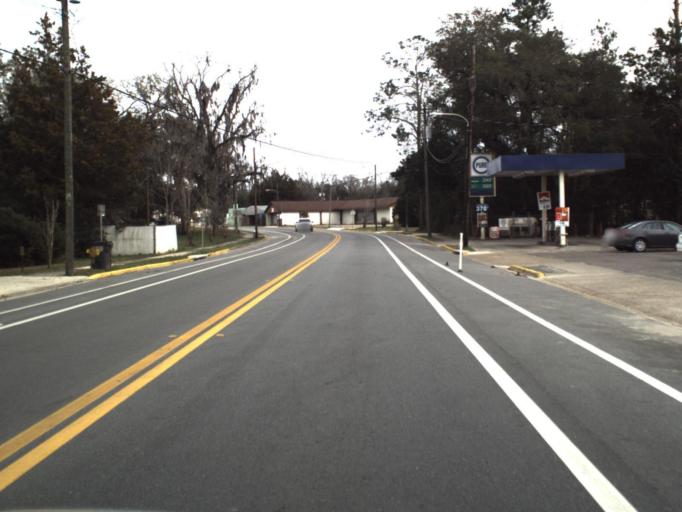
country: US
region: Florida
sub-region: Gulf County
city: Wewahitchka
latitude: 30.1137
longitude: -85.2031
